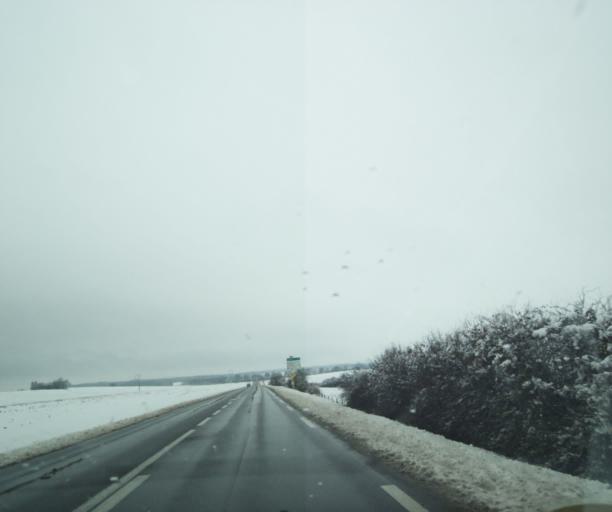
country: FR
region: Champagne-Ardenne
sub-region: Departement de la Haute-Marne
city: Montier-en-Der
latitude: 48.5159
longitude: 4.8074
